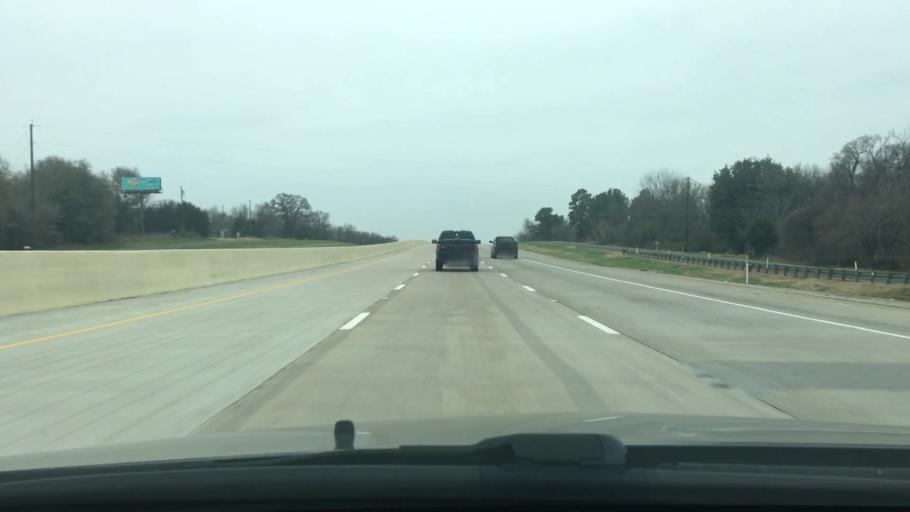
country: US
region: Texas
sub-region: Navarro County
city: Corsicana
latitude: 31.9612
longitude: -96.4205
